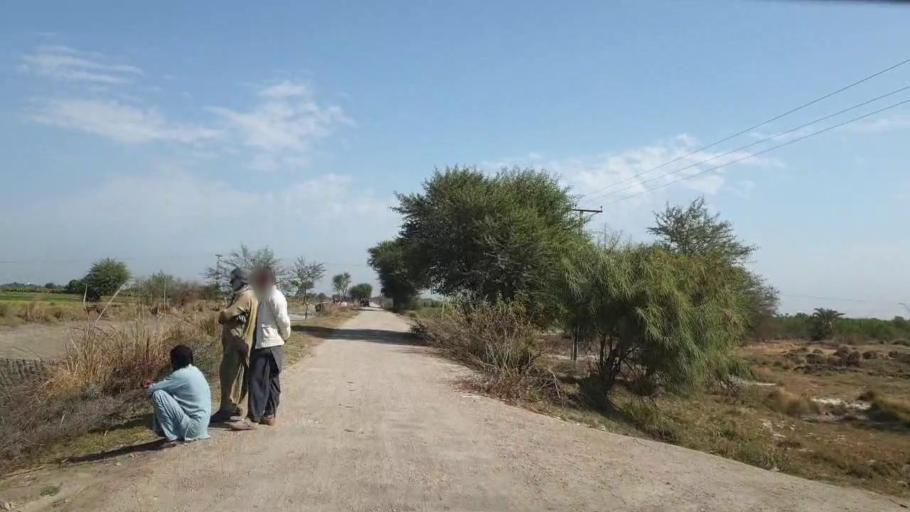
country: PK
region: Sindh
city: Matiari
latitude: 25.5588
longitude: 68.4684
